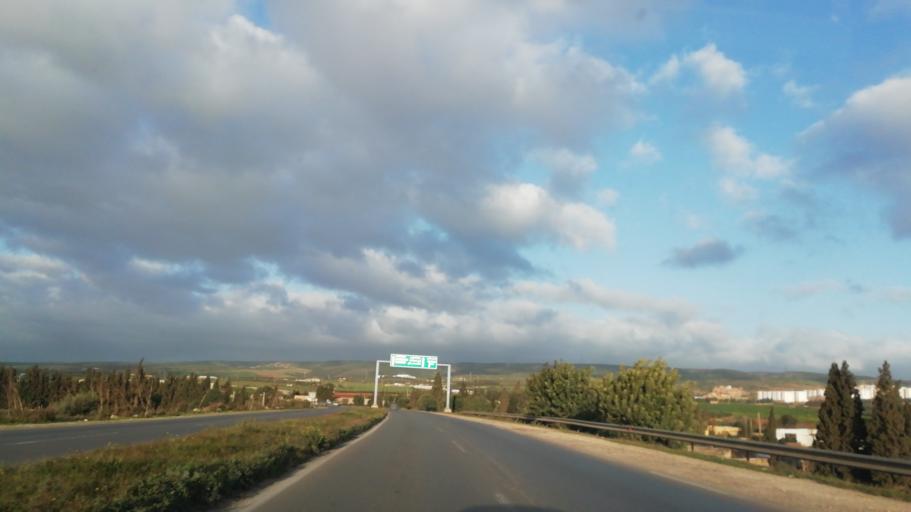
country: DZ
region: Oran
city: Mers el Kebir
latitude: 35.6071
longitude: -0.7434
